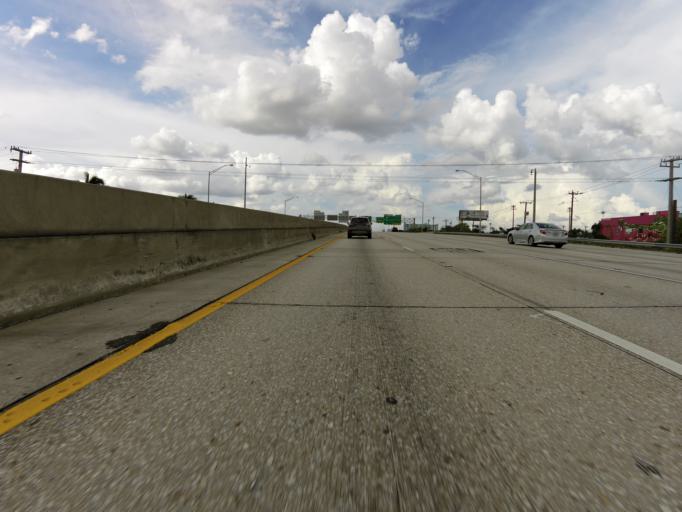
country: US
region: Florida
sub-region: Miami-Dade County
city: Allapattah
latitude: 25.8022
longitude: -80.2056
